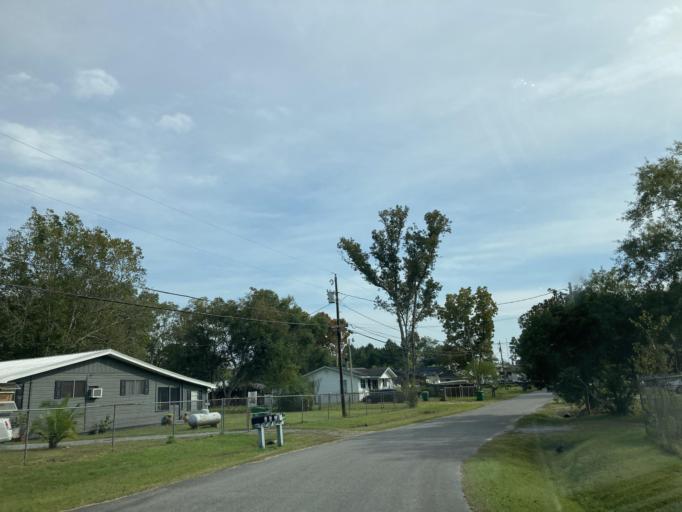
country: US
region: Mississippi
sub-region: Jackson County
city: Saint Martin
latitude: 30.4825
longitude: -88.8578
